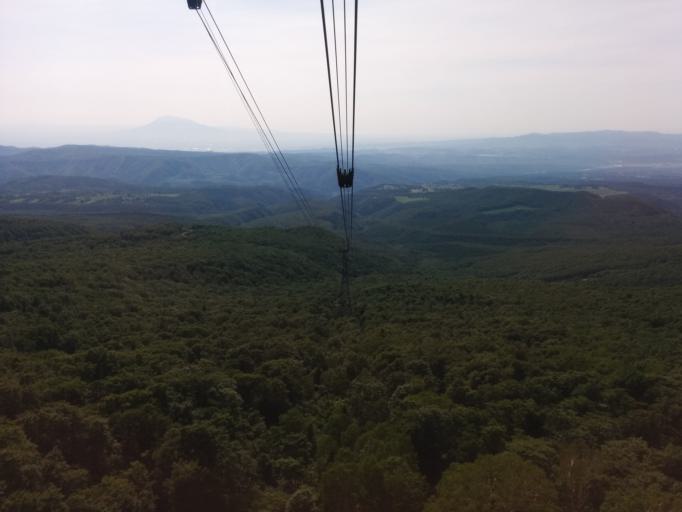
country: JP
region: Aomori
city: Aomori Shi
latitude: 40.6774
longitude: 140.8508
